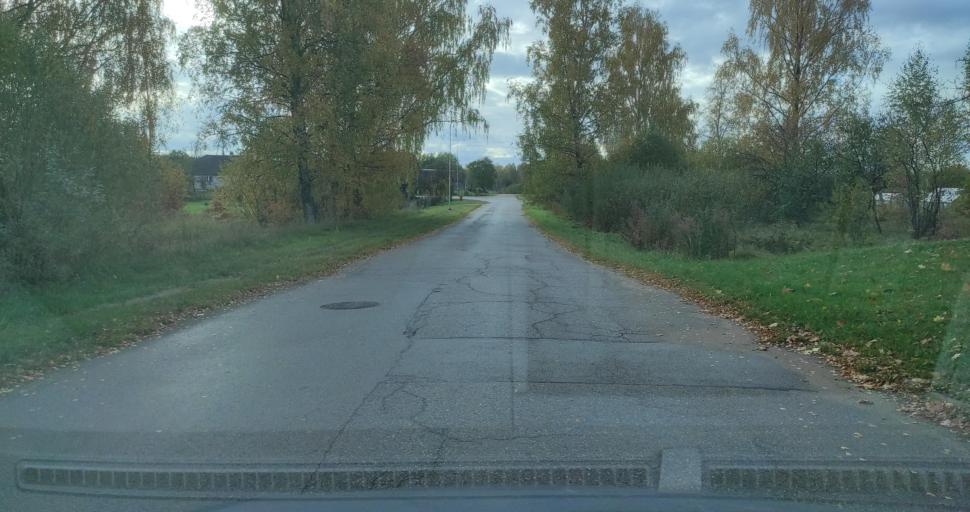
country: LV
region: Skrunda
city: Skrunda
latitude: 56.6723
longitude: 22.0008
